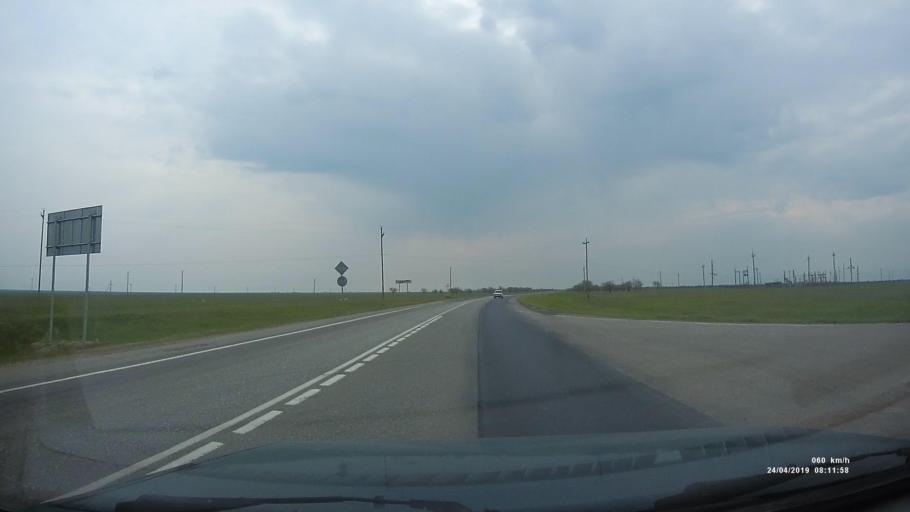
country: RU
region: Kalmykiya
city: Priyutnoye
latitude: 46.1033
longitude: 43.5346
